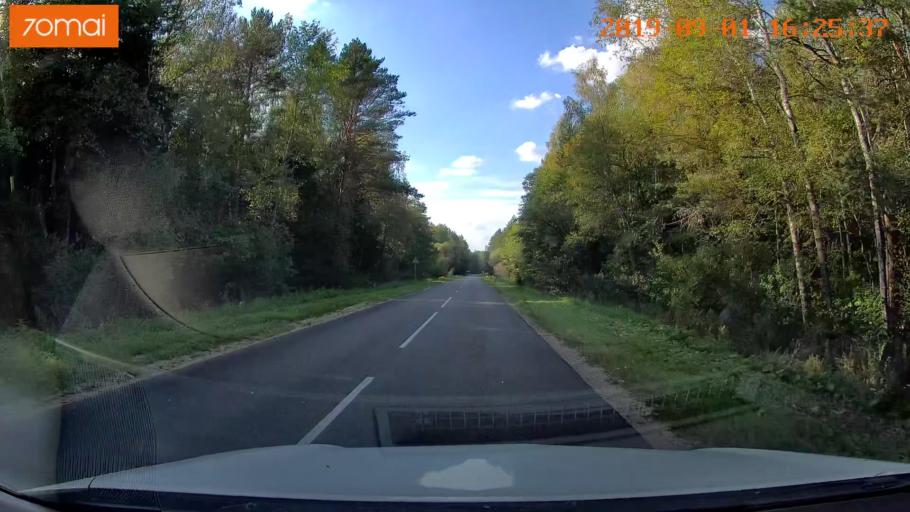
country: RU
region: Kaluga
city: Maloyaroslavets
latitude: 54.9048
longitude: 36.5147
